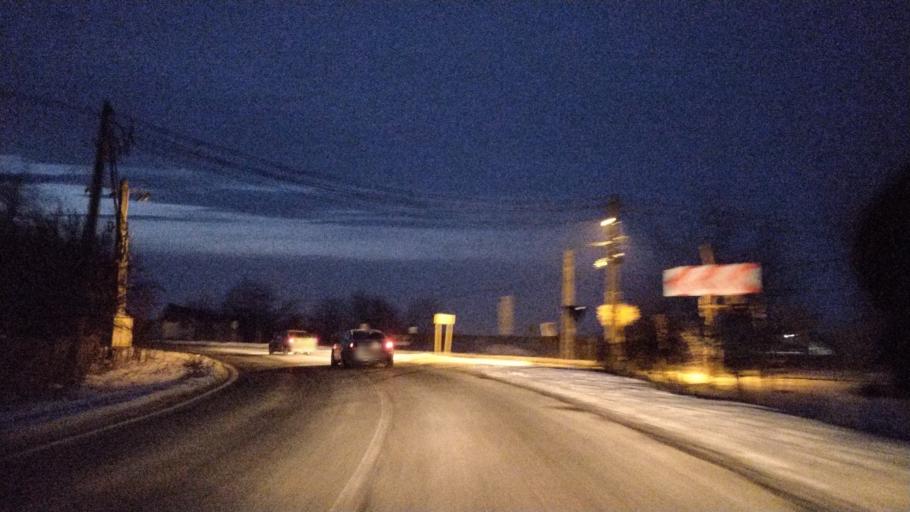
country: RO
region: Vrancea
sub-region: Comuna Milcovul
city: Milcovul
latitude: 45.6796
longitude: 27.2354
